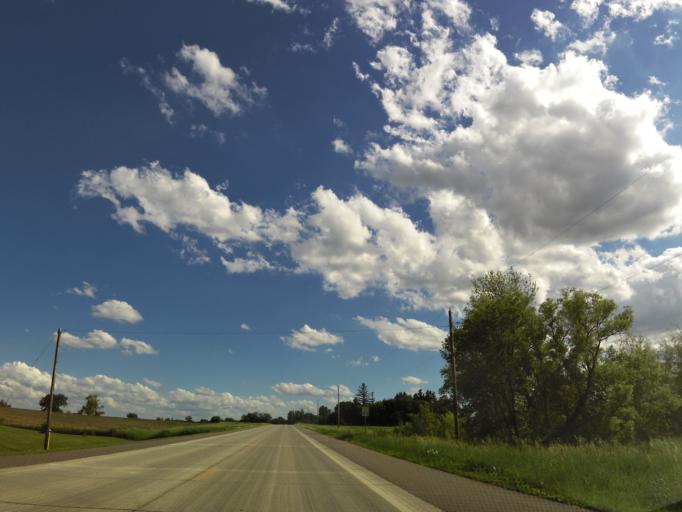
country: US
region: Minnesota
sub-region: Wright County
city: Cokato
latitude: 45.0627
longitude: -94.1905
